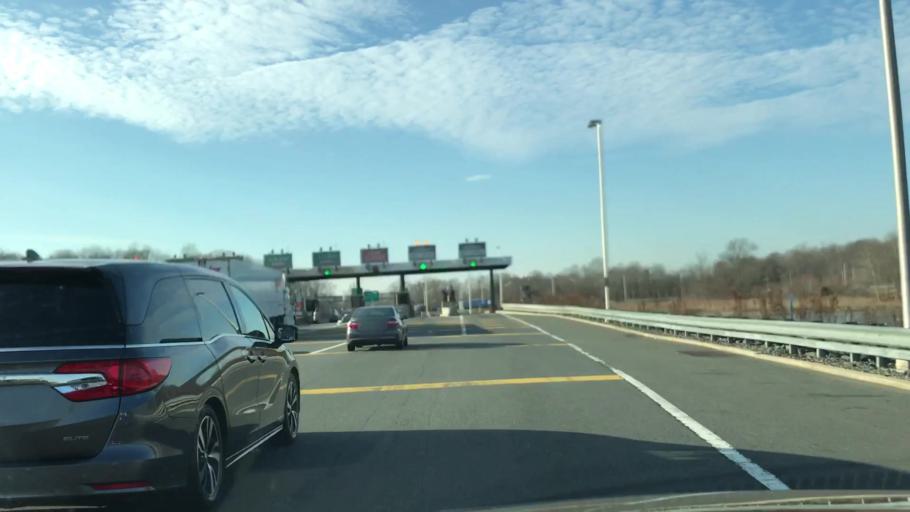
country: US
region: New Jersey
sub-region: Mercer County
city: Robbinsville
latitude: 40.1941
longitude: -74.6063
